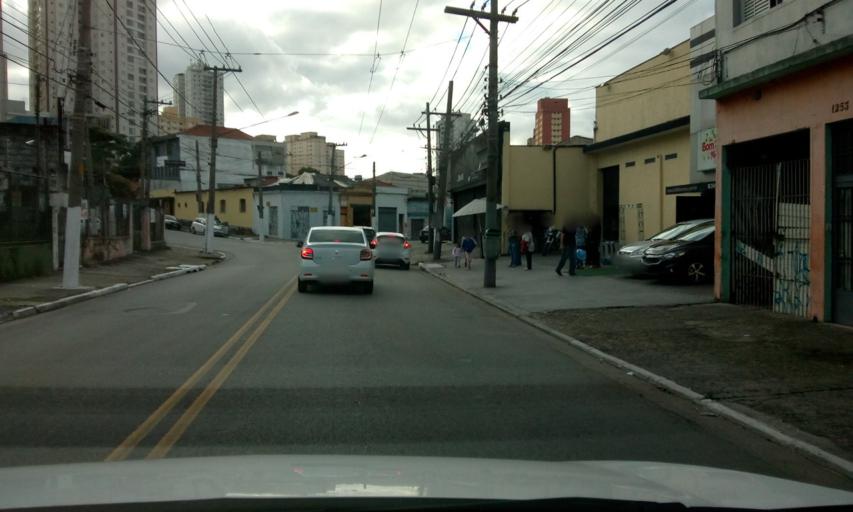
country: BR
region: Sao Paulo
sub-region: Sao Caetano Do Sul
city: Sao Caetano do Sul
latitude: -23.5431
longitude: -46.5475
